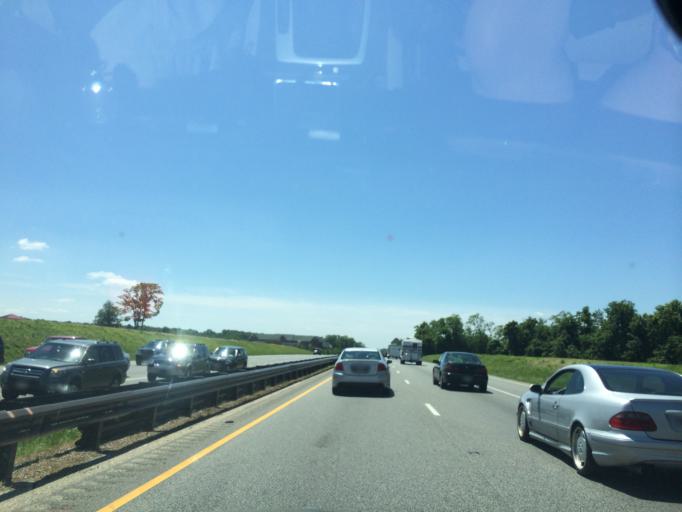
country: US
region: Maryland
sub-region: Talbot County
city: Easton
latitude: 38.7930
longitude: -76.0602
